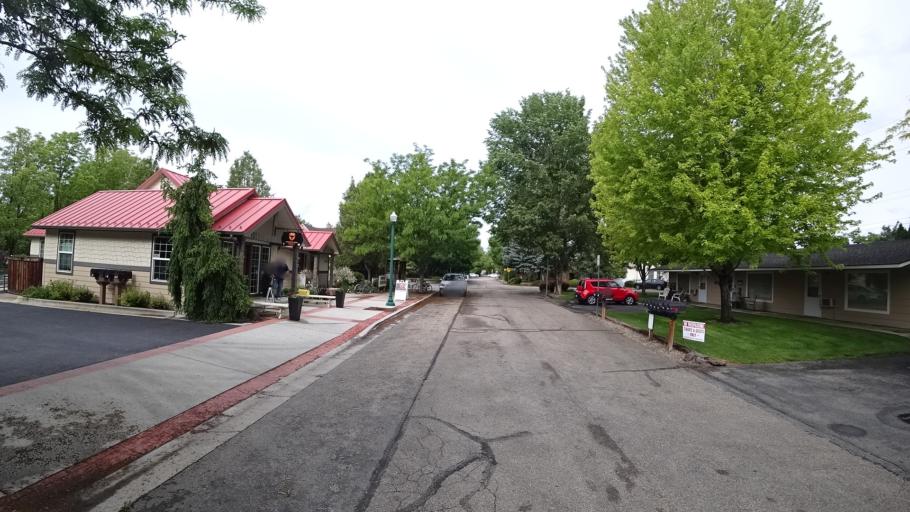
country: US
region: Idaho
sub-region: Ada County
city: Eagle
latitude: 43.6942
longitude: -116.3522
